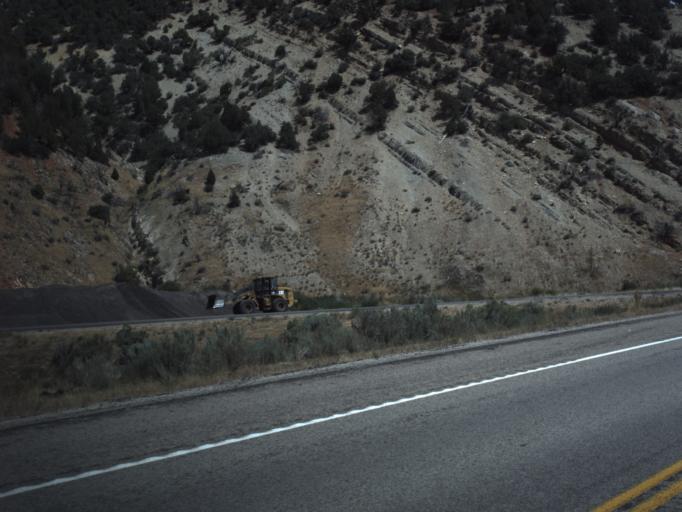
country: US
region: Utah
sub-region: Utah County
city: Woodland Hills
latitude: 39.9935
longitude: -111.4955
